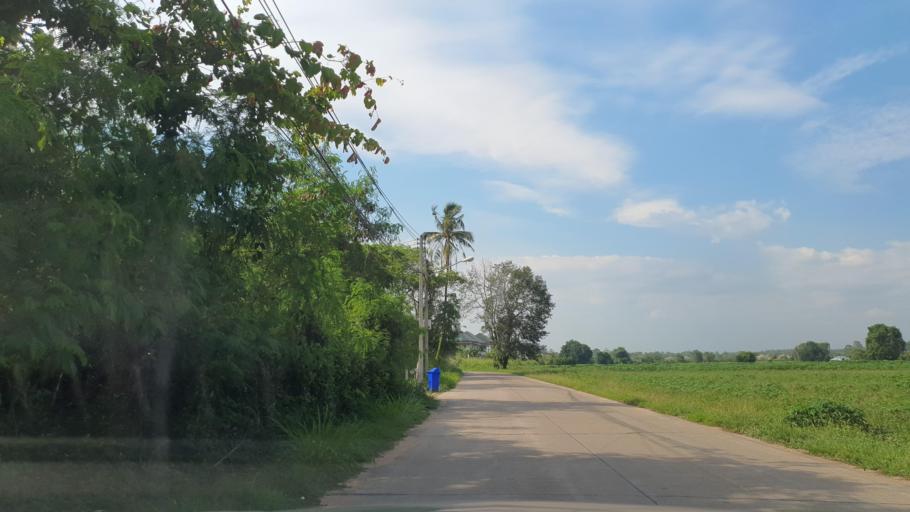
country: TH
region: Chon Buri
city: Sattahip
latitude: 12.7989
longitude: 100.9351
